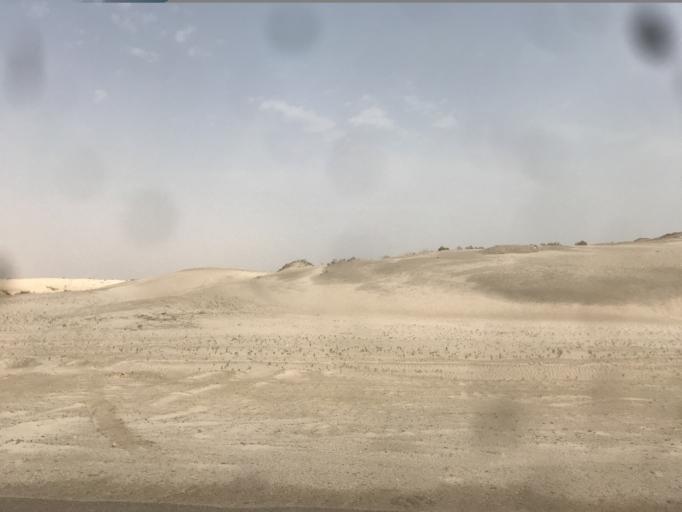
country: SA
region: Eastern Province
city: Abqaiq
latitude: 25.9058
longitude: 50.0107
